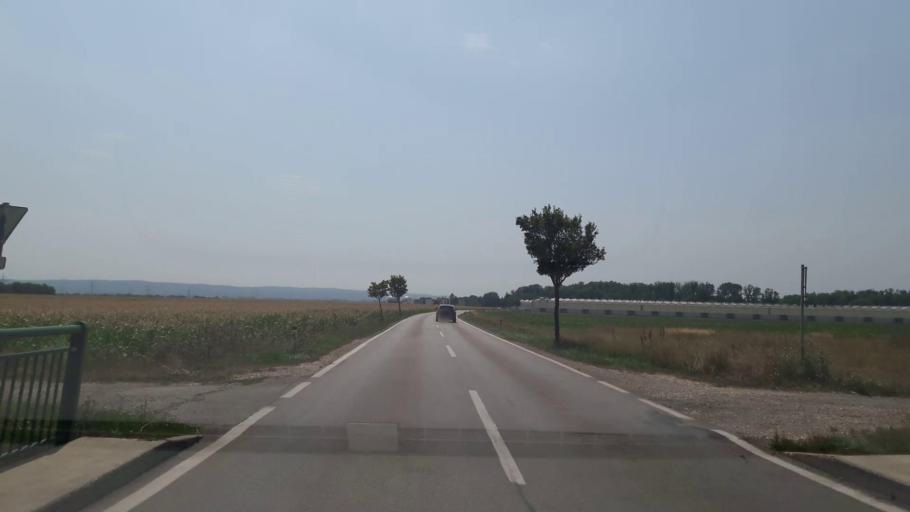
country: AT
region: Lower Austria
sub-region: Politischer Bezirk Bruck an der Leitha
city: Enzersdorf an der Fischa
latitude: 48.0619
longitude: 16.6097
